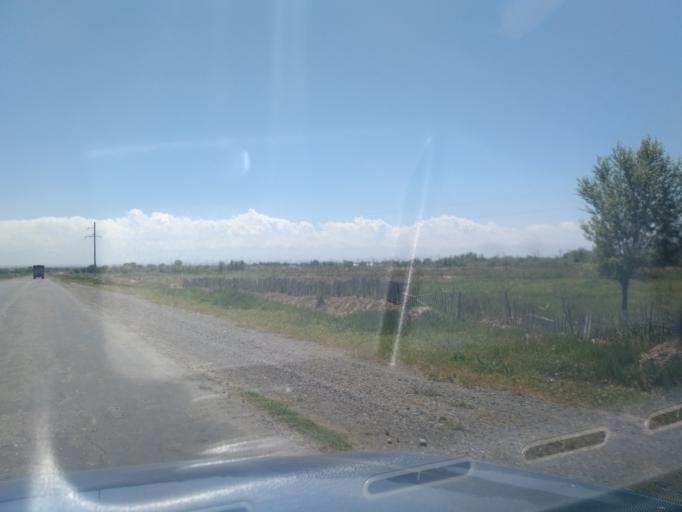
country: TJ
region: Viloyati Sughd
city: Zafarobod
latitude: 40.2285
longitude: 68.8492
